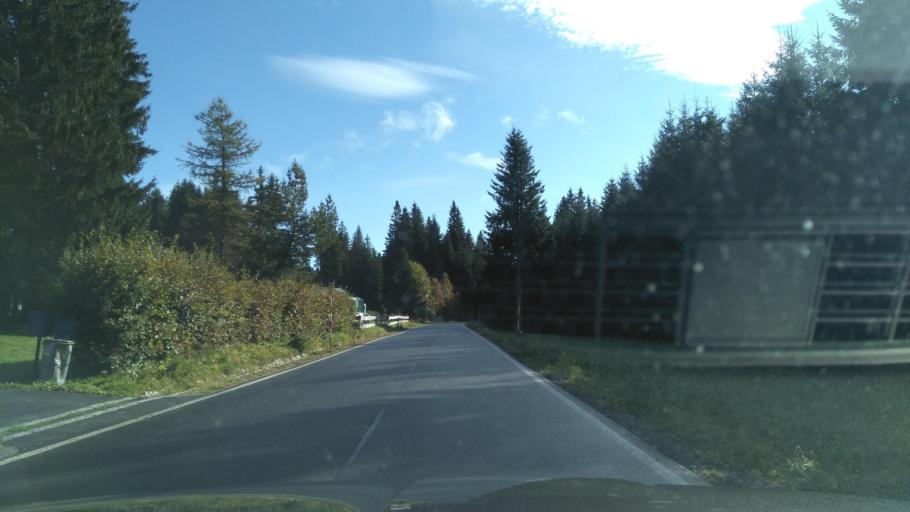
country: CZ
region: Plzensky
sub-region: Okres Klatovy
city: Kasperske Hory
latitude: 49.0295
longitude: 13.5261
